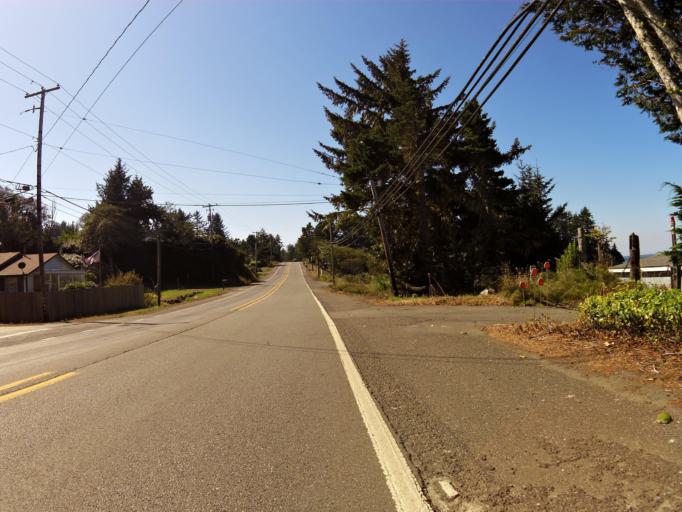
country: US
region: Oregon
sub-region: Coos County
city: Barview
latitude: 43.3589
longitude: -124.3079
